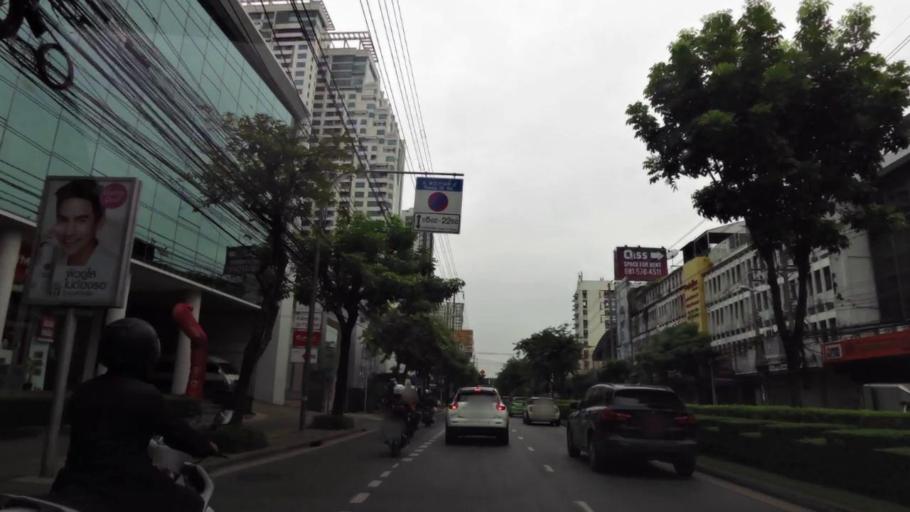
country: TH
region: Bangkok
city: Khlong Toei
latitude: 13.7128
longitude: 100.5872
